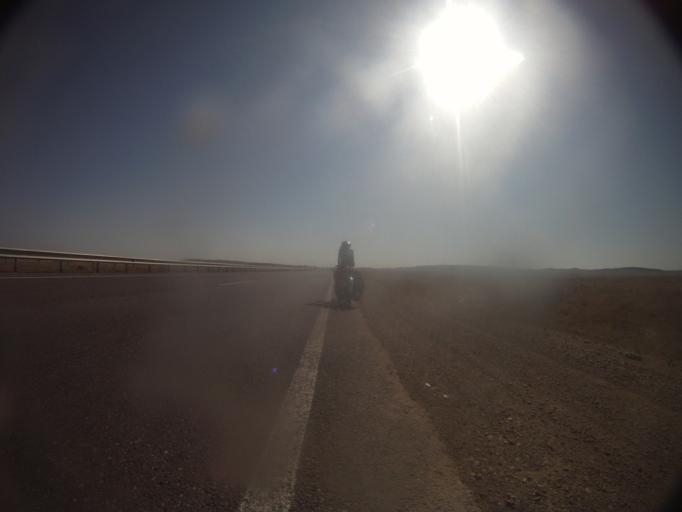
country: KZ
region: Zhambyl
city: Taraz
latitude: 42.7329
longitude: 70.9088
